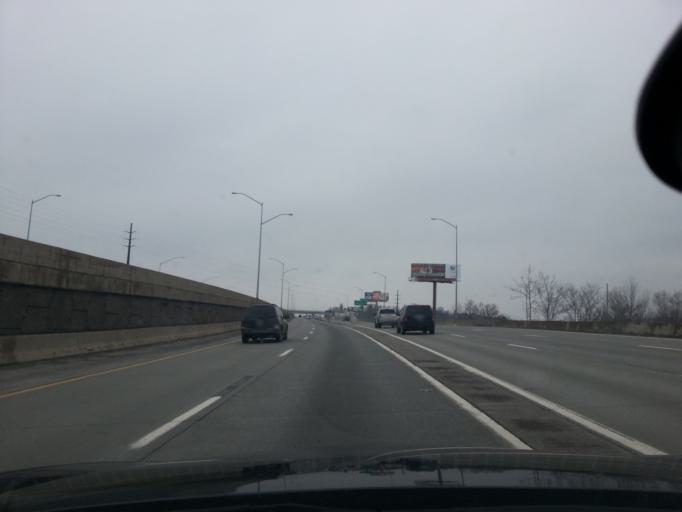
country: US
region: Pennsylvania
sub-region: Lackawanna County
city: Dunmore
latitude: 41.4123
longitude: -75.6172
